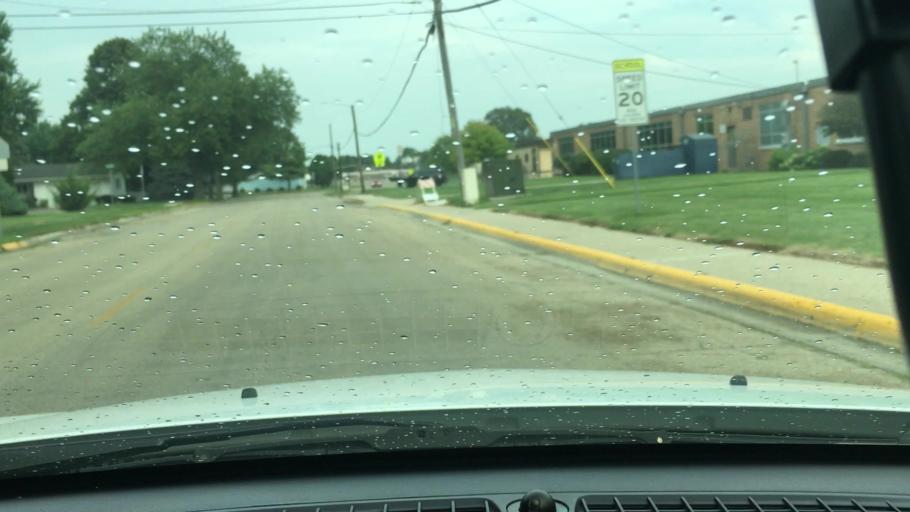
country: US
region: Illinois
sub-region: Ogle County
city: Rochelle
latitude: 41.9304
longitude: -89.0627
